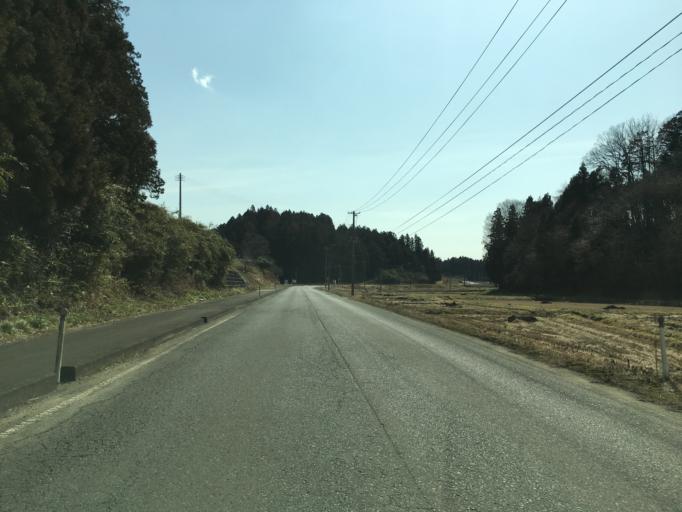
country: JP
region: Fukushima
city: Ishikawa
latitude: 37.1345
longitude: 140.4091
